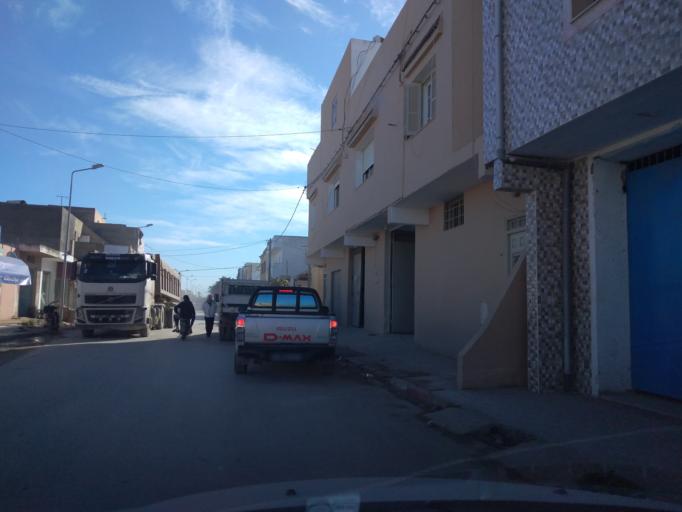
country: TN
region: Ariana
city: Qal'at al Andalus
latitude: 37.0614
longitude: 10.1186
